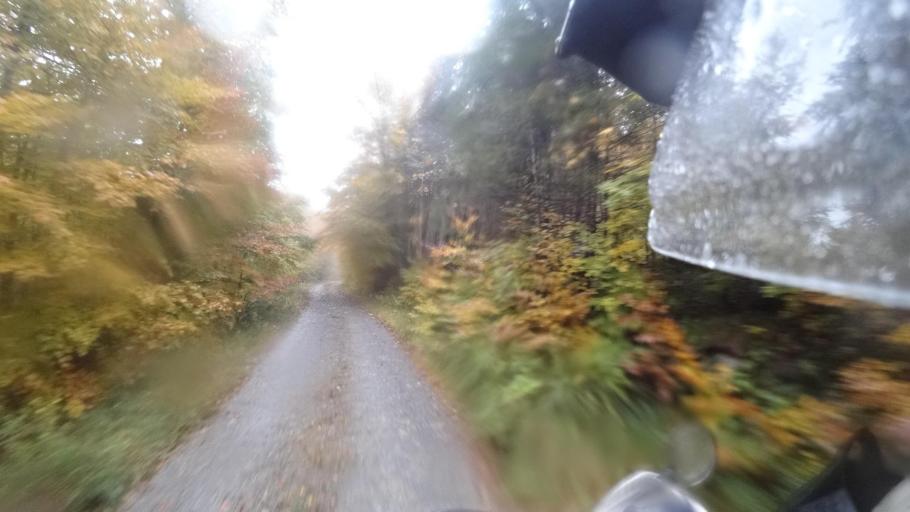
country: HR
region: Primorsko-Goranska
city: Vrbovsko
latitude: 45.3534
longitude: 15.0725
